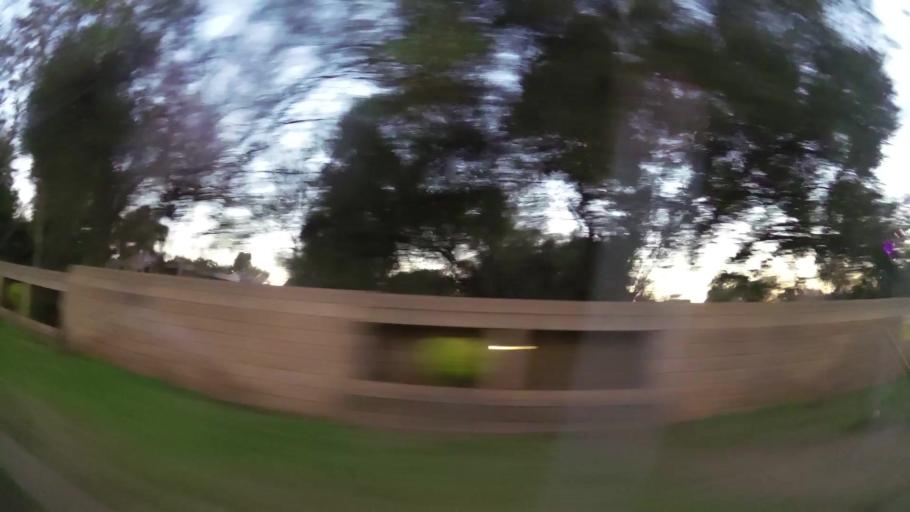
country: ZA
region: Gauteng
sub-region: City of Tshwane Metropolitan Municipality
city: Centurion
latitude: -25.8531
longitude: 28.1332
